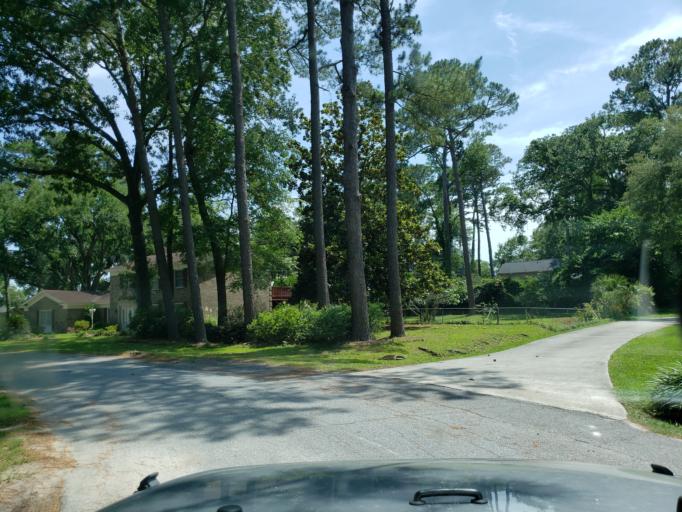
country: US
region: Georgia
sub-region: Chatham County
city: Whitemarsh Island
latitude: 32.0262
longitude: -81.0043
